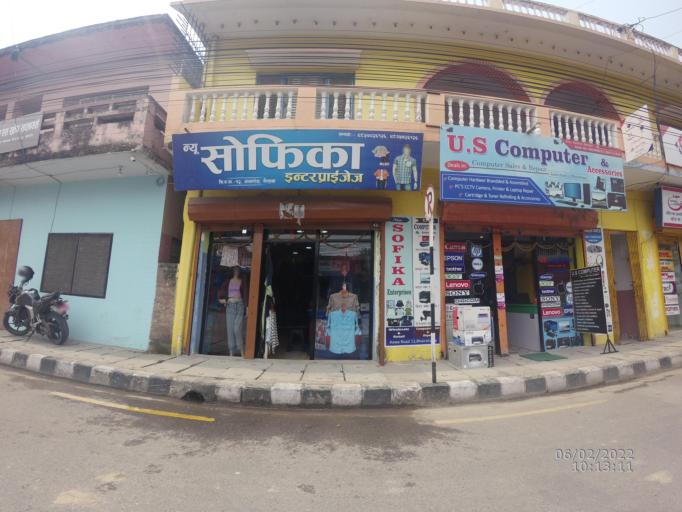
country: NP
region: Western Region
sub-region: Lumbini Zone
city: Bhairahawa
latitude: 27.5087
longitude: 83.4531
